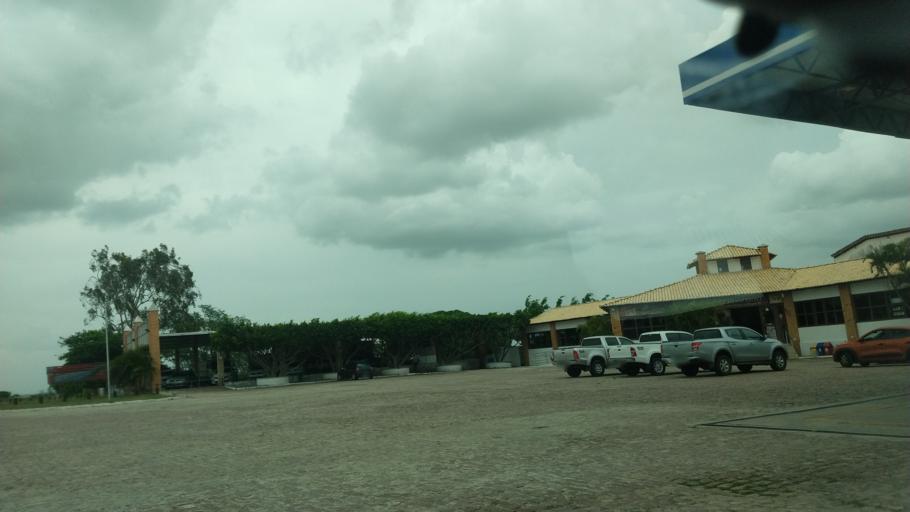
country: BR
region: Rio Grande do Norte
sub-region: Tangara
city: Tangara
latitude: -6.1733
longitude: -35.7649
